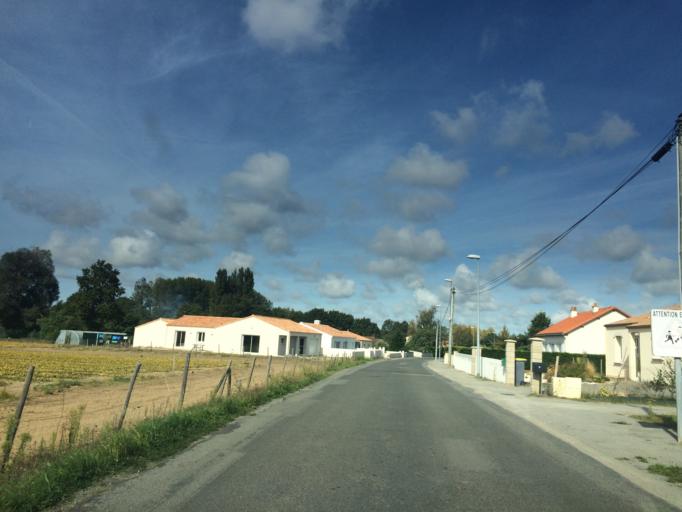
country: FR
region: Pays de la Loire
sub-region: Departement de la Loire-Atlantique
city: Chemere
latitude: 47.1276
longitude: -1.9227
